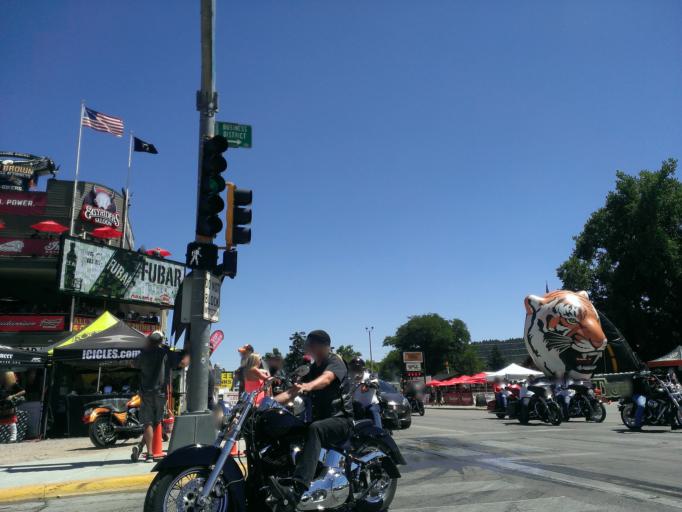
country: US
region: South Dakota
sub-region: Meade County
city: Sturgis
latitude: 44.4156
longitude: -103.5091
